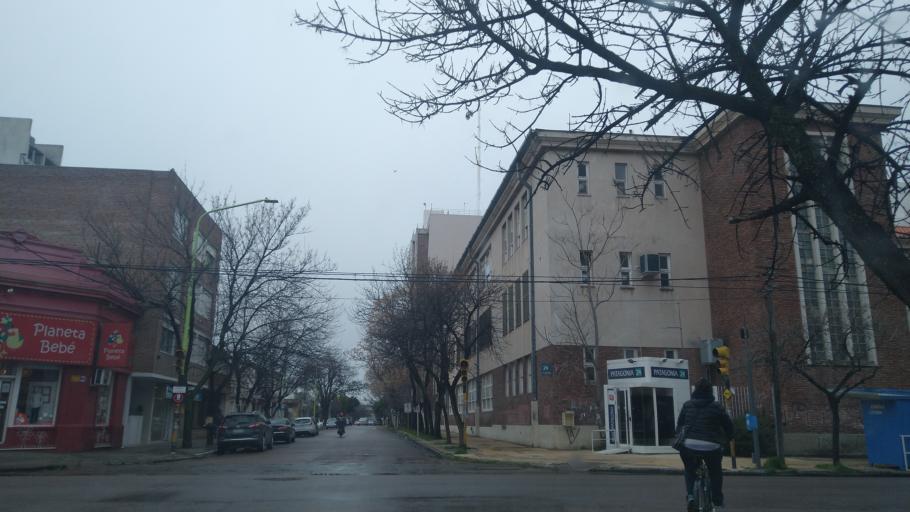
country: AR
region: Buenos Aires
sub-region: Partido de Bahia Blanca
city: Bahia Blanca
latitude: -38.7110
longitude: -62.2657
